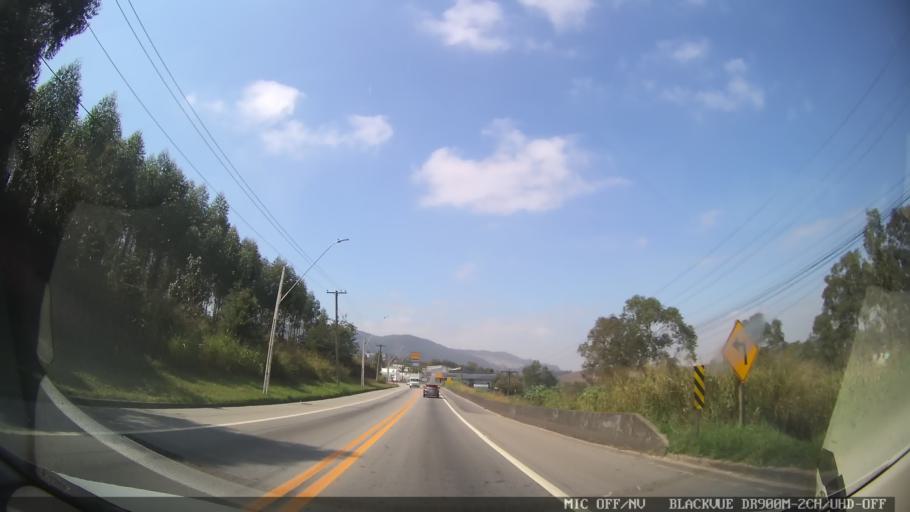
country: BR
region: Sao Paulo
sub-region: Caieiras
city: Caieiras
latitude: -23.3836
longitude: -46.7349
